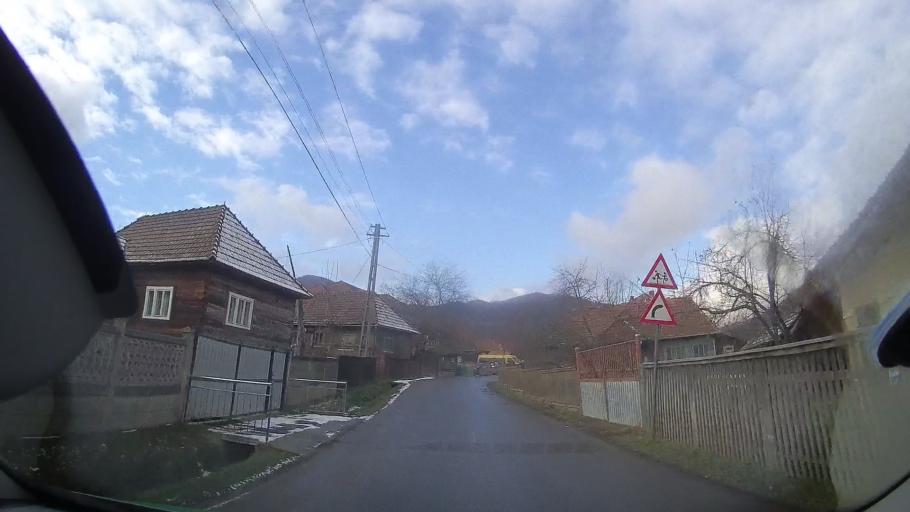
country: RO
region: Alba
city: Salciua de Sus
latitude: 46.4303
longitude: 23.4395
